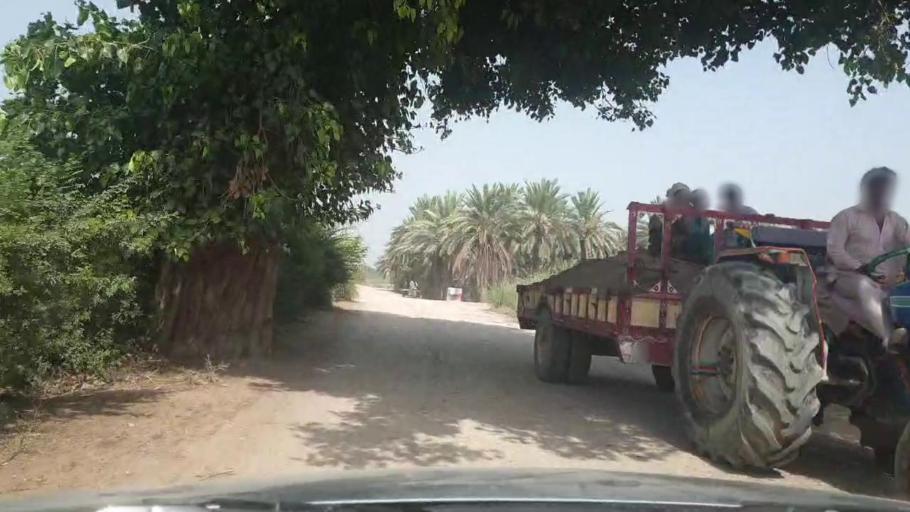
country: PK
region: Sindh
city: Pano Aqil
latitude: 27.8579
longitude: 69.0981
